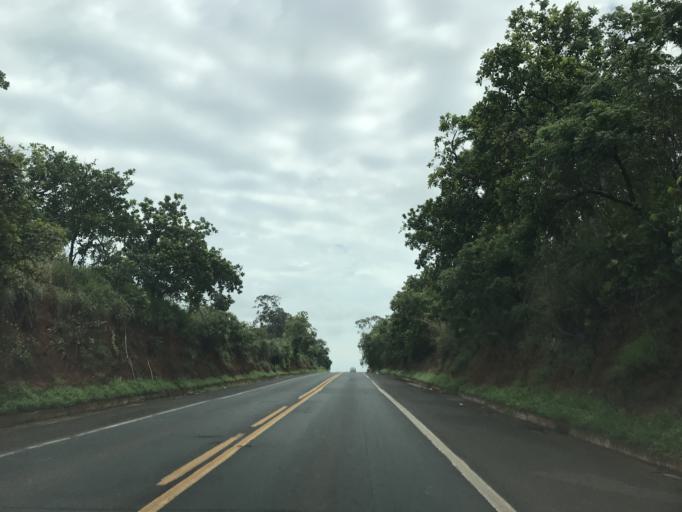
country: BR
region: Minas Gerais
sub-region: Frutal
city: Frutal
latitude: -19.9241
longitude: -48.9593
